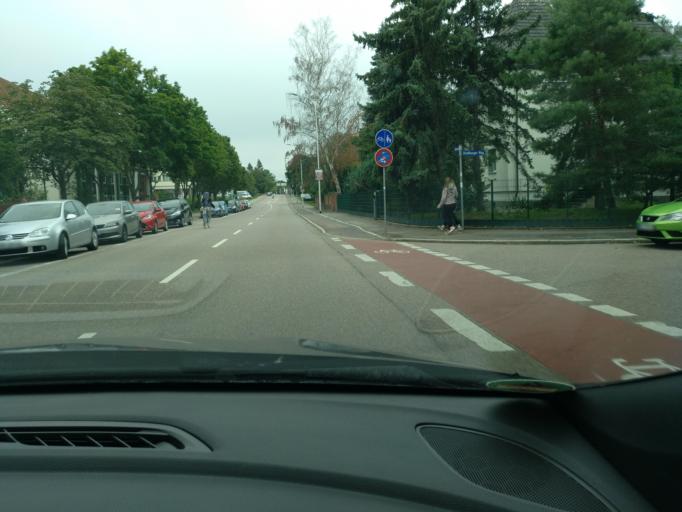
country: DE
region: Saxony-Anhalt
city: Halle Neustadt
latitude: 51.4997
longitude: 11.9403
